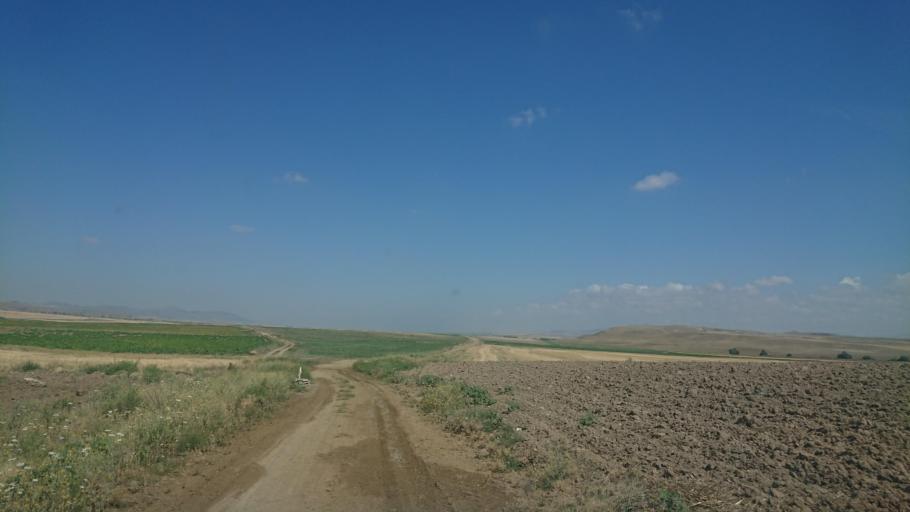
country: TR
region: Aksaray
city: Sariyahsi
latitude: 38.9632
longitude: 33.9272
